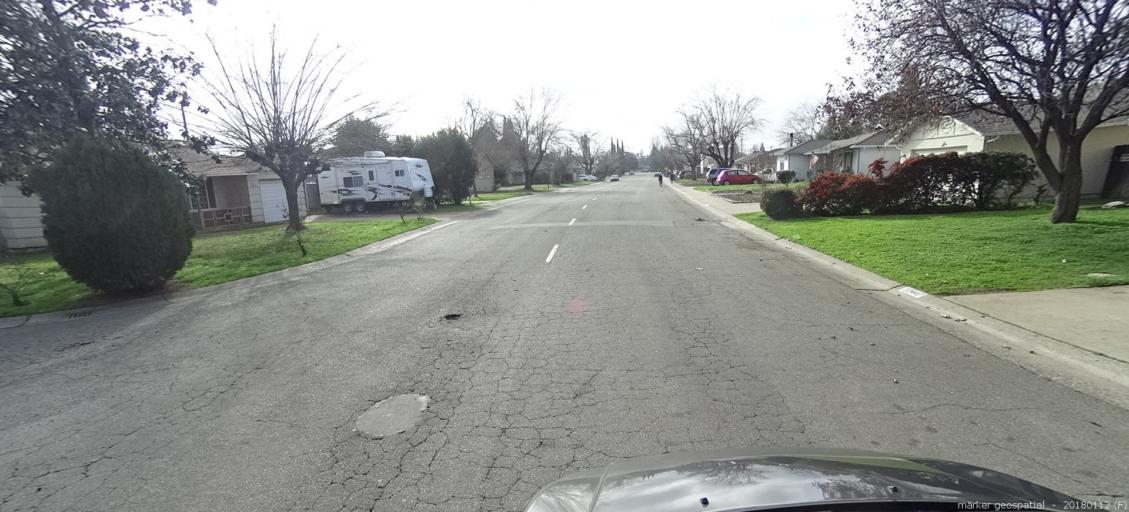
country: US
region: California
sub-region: Sacramento County
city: Rancho Cordova
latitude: 38.5965
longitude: -121.3022
